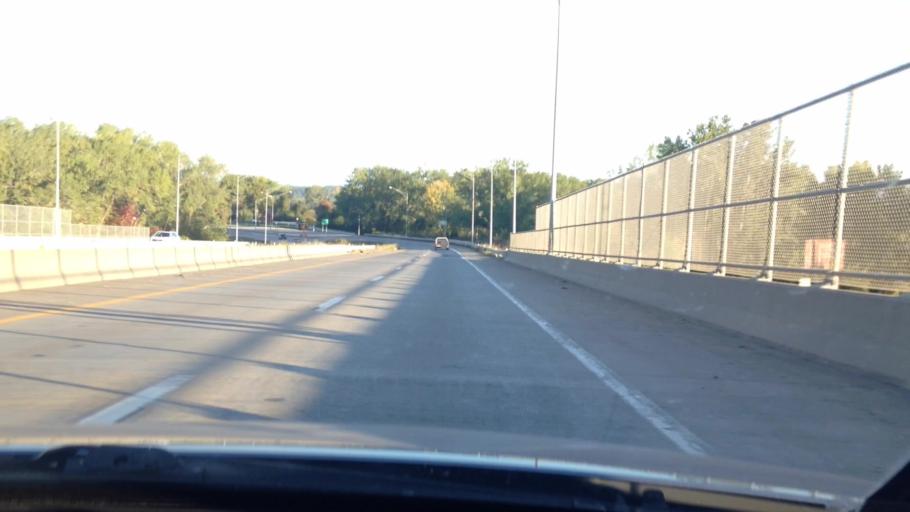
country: US
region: Missouri
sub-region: Clay County
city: Claycomo
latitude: 39.1564
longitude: -94.4838
